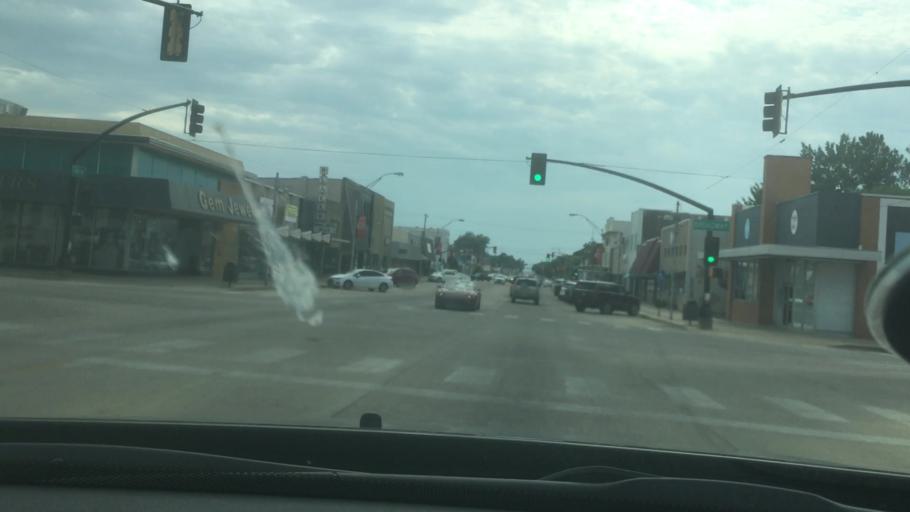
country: US
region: Oklahoma
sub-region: Pontotoc County
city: Ada
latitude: 34.7745
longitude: -96.6783
